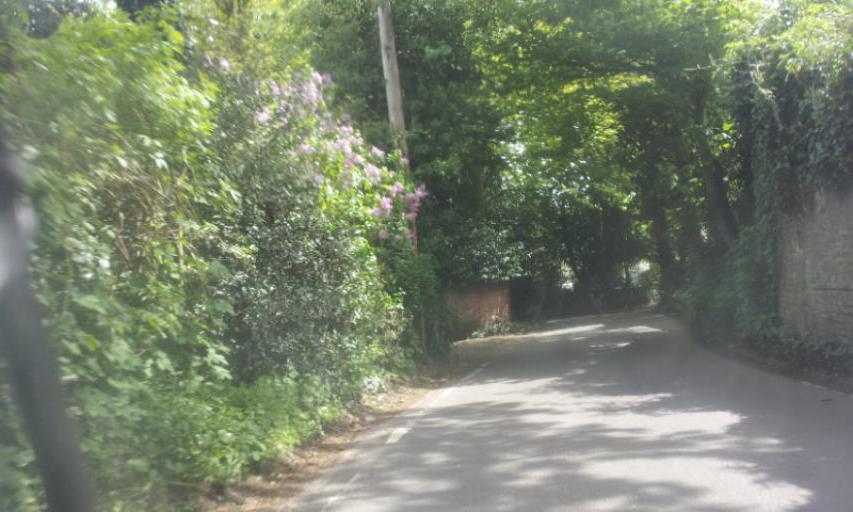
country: GB
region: England
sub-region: Kent
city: Swanley
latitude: 51.4044
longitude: 0.1969
